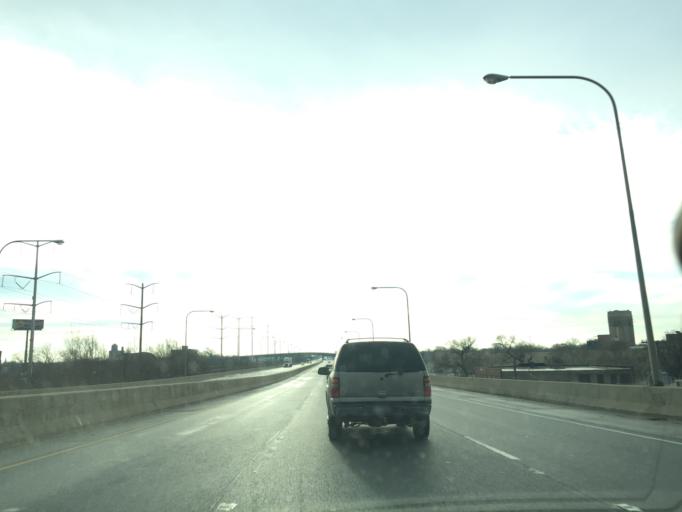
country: US
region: Illinois
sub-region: Cook County
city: Chicago
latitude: 41.7547
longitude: -87.5928
